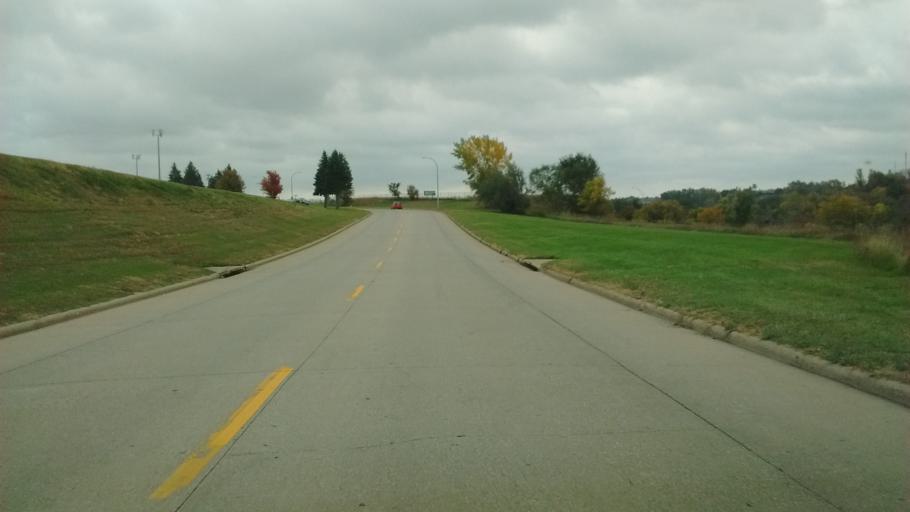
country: US
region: Iowa
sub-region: Woodbury County
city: Sergeant Bluff
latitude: 42.4459
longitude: -96.3560
